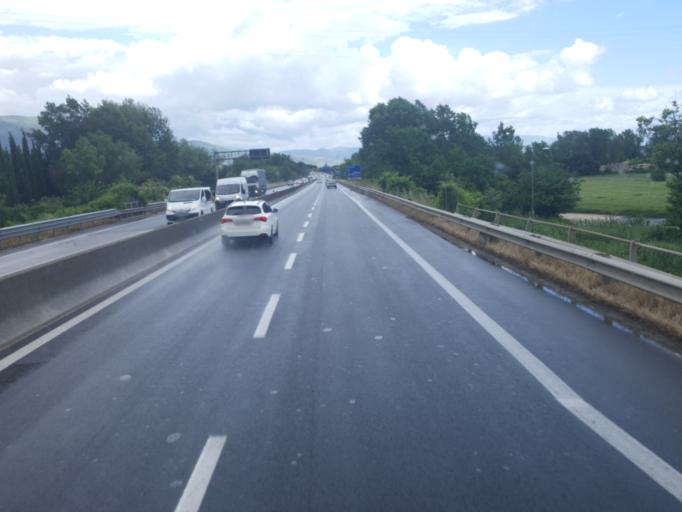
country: IT
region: Umbria
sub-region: Provincia di Perugia
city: Bastia umbra
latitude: 43.0650
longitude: 12.5403
